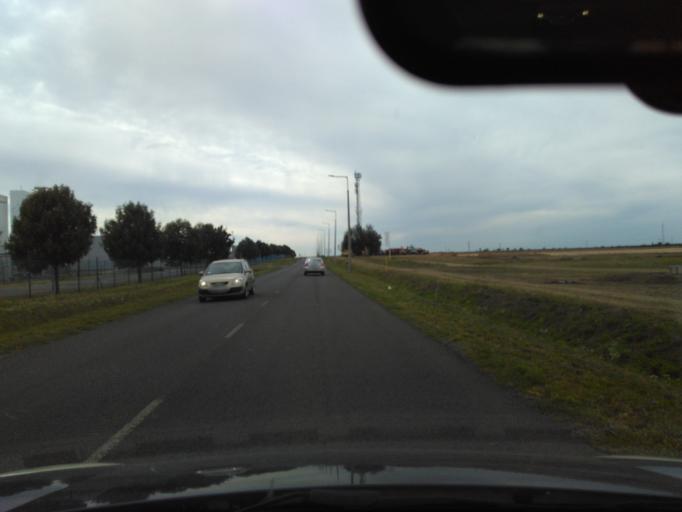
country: HU
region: Heves
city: Hatvan
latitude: 47.6715
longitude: 19.6477
